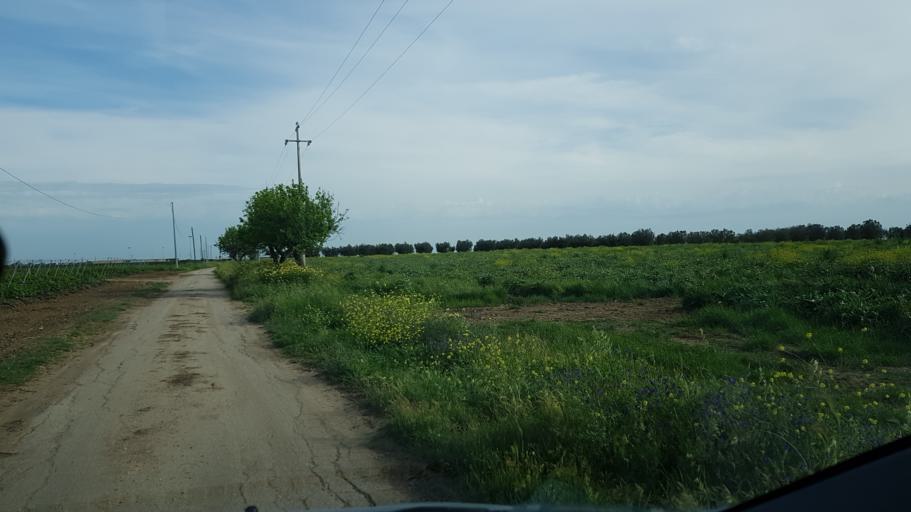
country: IT
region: Apulia
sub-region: Provincia di Brindisi
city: Cellino San Marco
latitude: 40.5092
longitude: 17.9633
